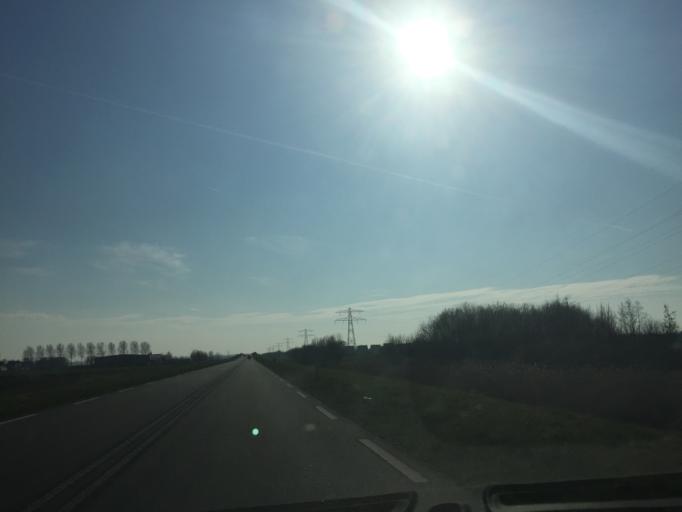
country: NL
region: South Holland
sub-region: Gemeente Hillegom
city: Hillegom
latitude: 52.2863
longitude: 4.6075
